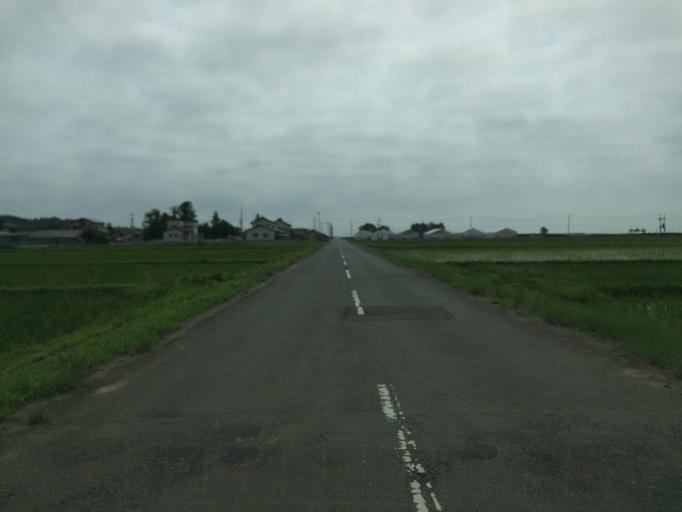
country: JP
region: Fukushima
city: Namie
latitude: 37.7029
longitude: 140.9804
